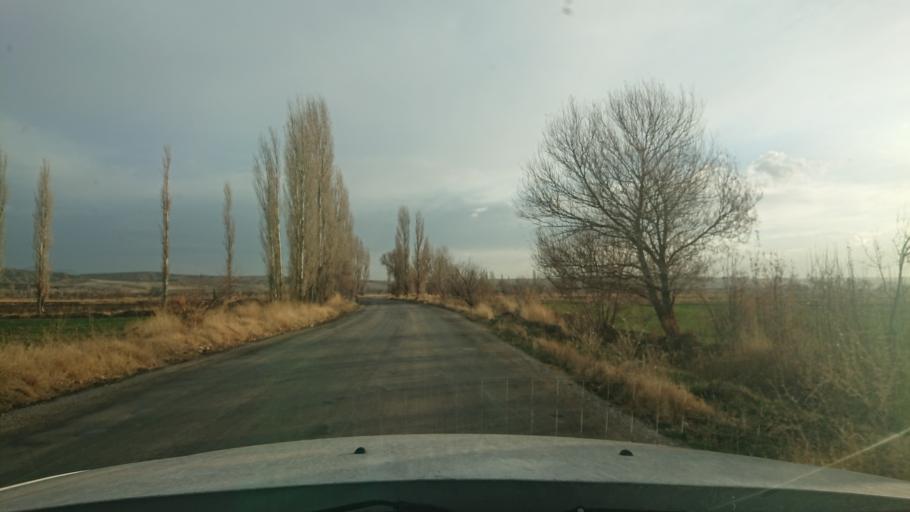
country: TR
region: Aksaray
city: Acipinar
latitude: 38.4768
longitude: 33.8763
